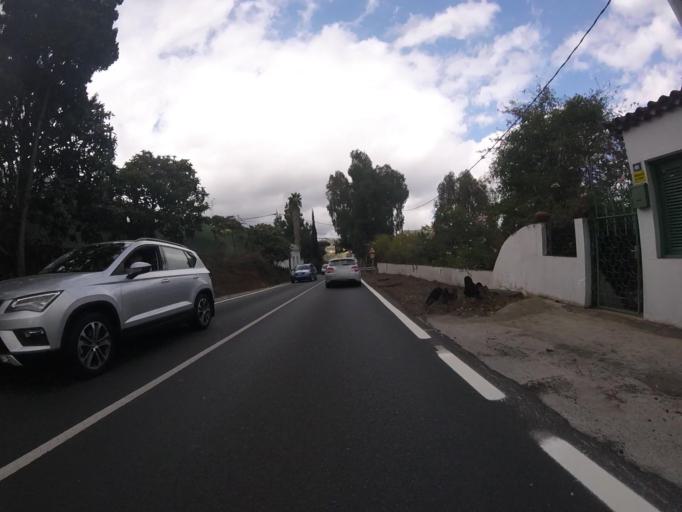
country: ES
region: Canary Islands
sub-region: Provincia de Las Palmas
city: Vega de San Mateo
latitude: 28.0175
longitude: -15.5250
